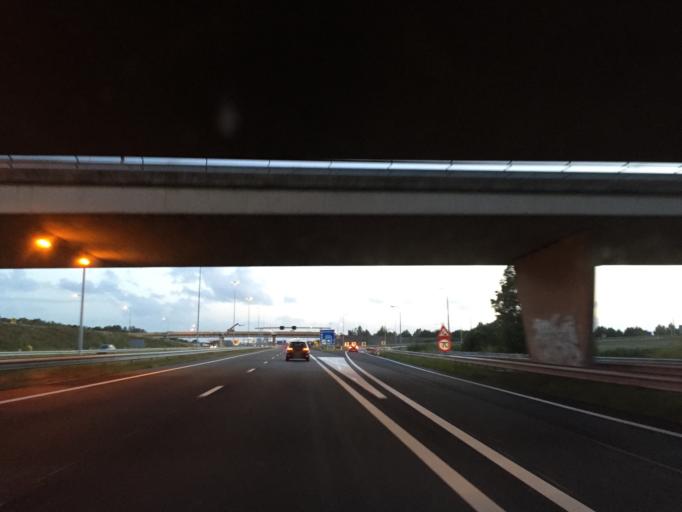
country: NL
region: Flevoland
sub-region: Gemeente Almere
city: Almere Stad
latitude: 52.3432
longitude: 5.1767
